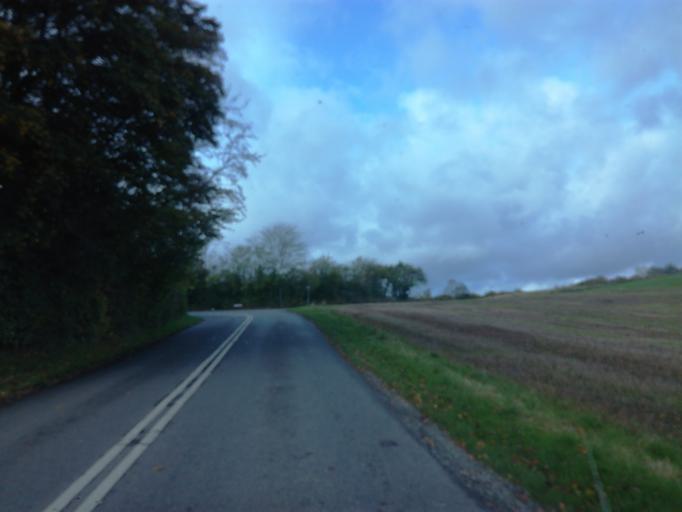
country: DK
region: South Denmark
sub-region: Vejle Kommune
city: Brejning
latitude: 55.6666
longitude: 9.6504
